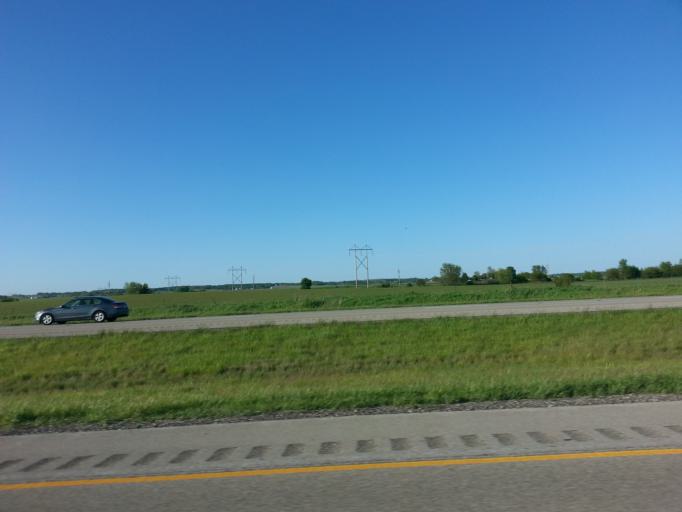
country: US
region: Illinois
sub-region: McLean County
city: Downs
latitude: 40.3719
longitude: -88.8364
